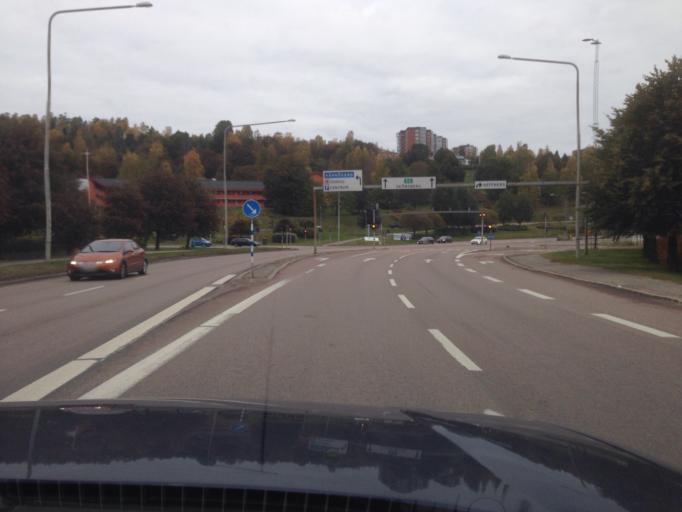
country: SE
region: Vaesternorrland
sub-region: Sundsvalls Kommun
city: Sundsvall
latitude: 62.3933
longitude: 17.3130
